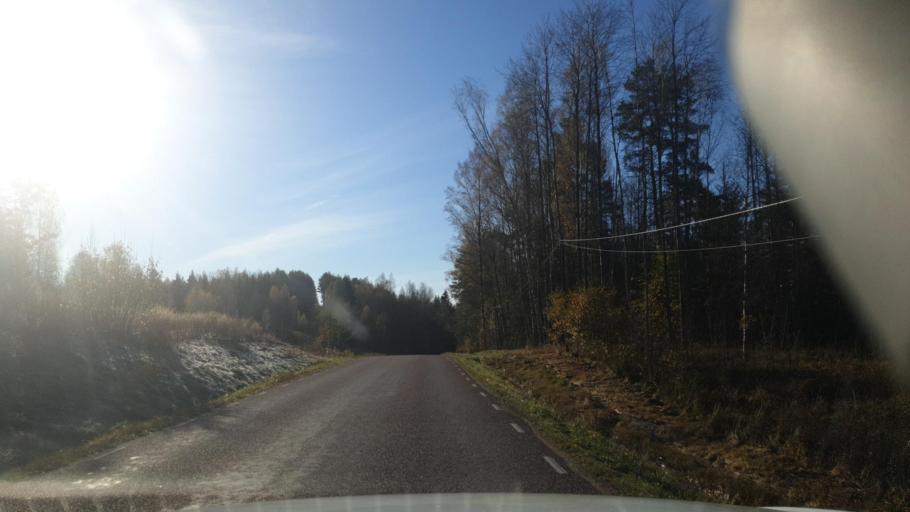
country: SE
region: Vaermland
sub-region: Grums Kommun
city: Grums
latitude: 59.4064
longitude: 13.0715
